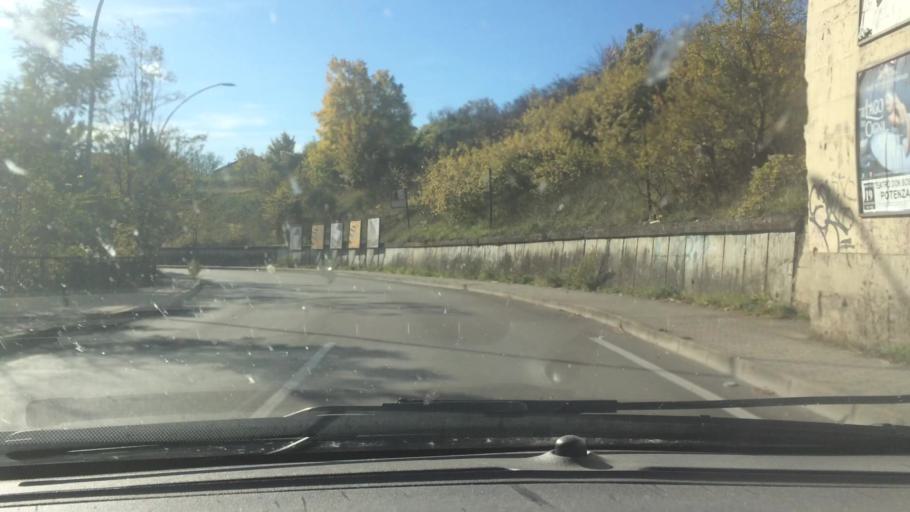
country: IT
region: Basilicate
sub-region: Provincia di Potenza
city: Potenza
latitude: 40.6437
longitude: 15.7961
